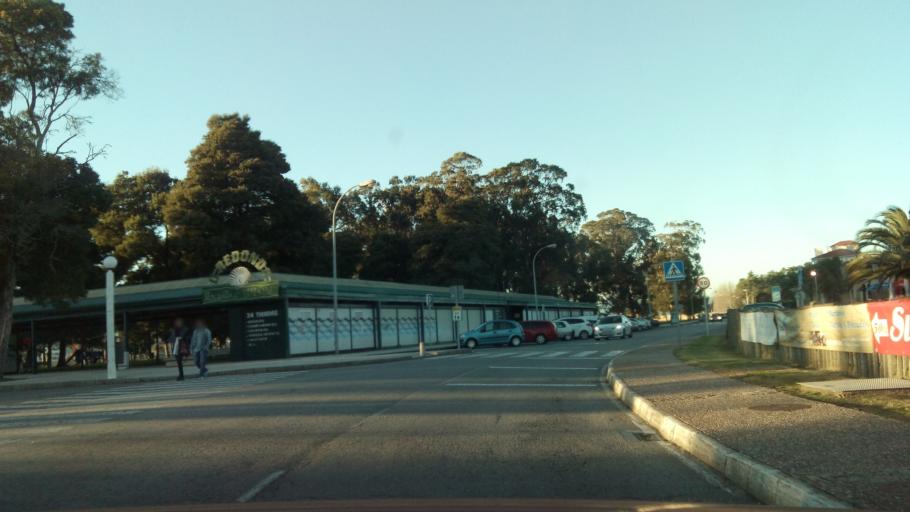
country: ES
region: Galicia
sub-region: Provincia de Pontevedra
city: O Grove
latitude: 42.4836
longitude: -8.8511
